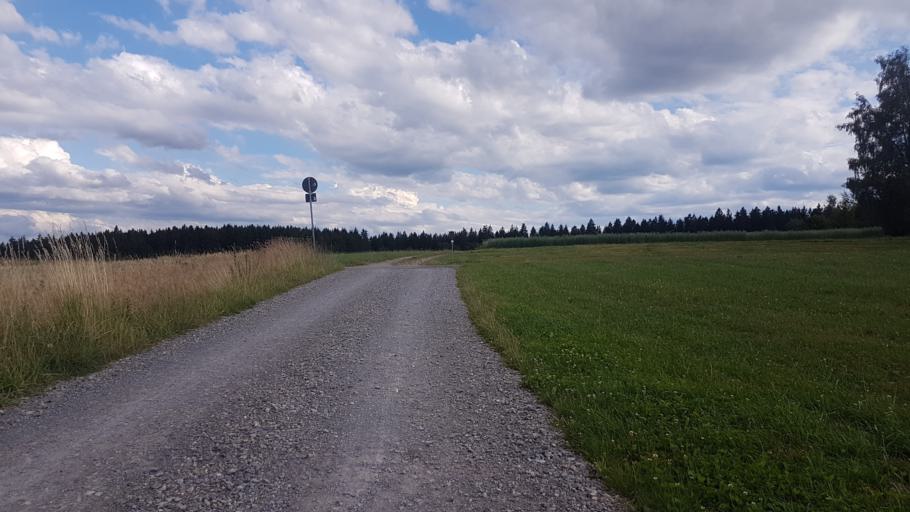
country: DE
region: Baden-Wuerttemberg
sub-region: Freiburg Region
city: Monchweiler
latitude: 48.0635
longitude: 8.4101
